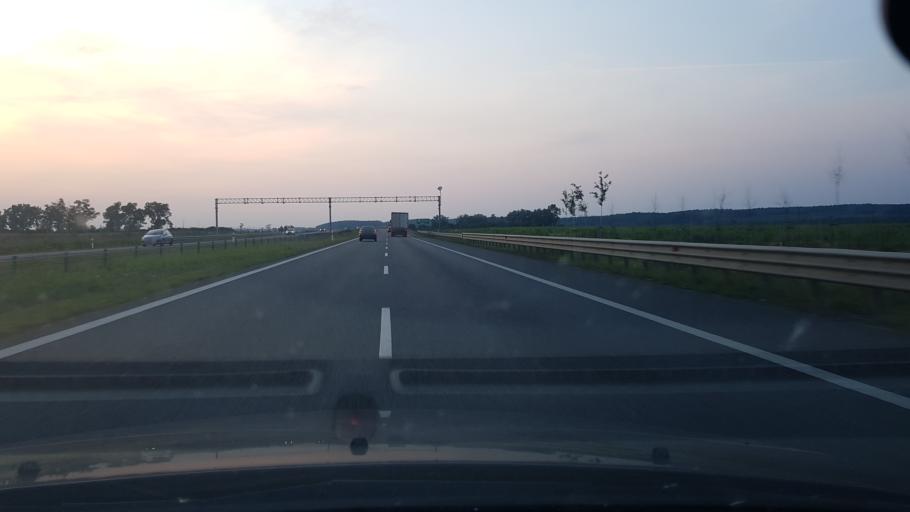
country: PL
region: Warmian-Masurian Voivodeship
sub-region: Powiat nidzicki
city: Nidzica
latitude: 53.3917
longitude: 20.3671
